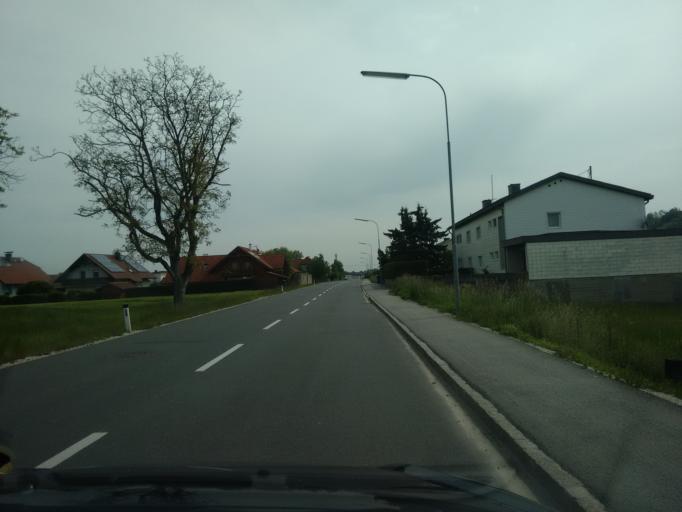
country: AT
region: Upper Austria
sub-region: Politischer Bezirk Linz-Land
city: Horsching
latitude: 48.1844
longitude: 14.1757
